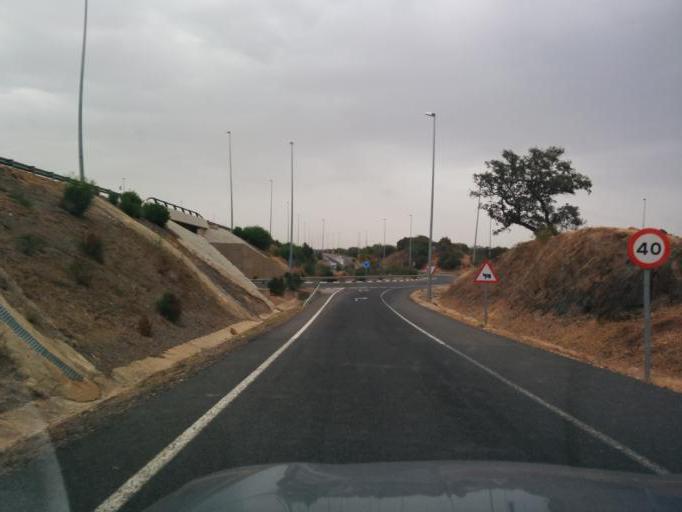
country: ES
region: Andalusia
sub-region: Provincia de Huelva
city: Ayamonte
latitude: 37.2387
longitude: -7.4059
